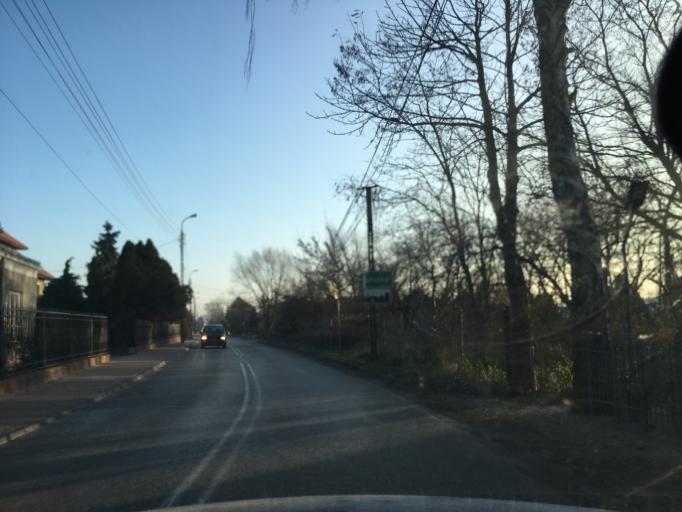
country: PL
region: Masovian Voivodeship
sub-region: Powiat piaseczynski
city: Piaseczno
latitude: 52.0692
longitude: 20.9882
